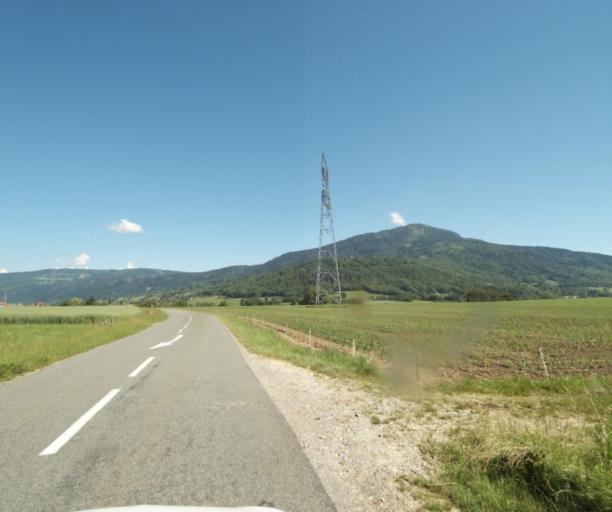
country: FR
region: Rhone-Alpes
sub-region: Departement de la Haute-Savoie
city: Loisin
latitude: 46.2657
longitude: 6.3300
